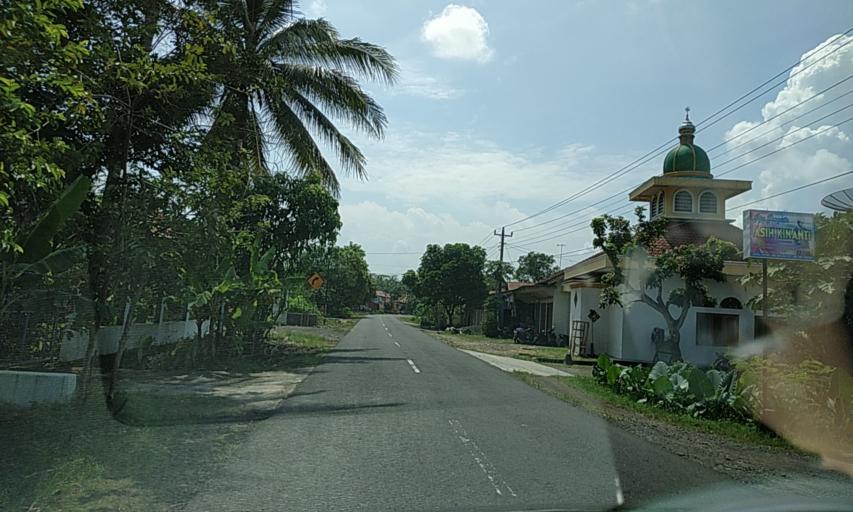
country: ID
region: Central Java
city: Mulyosari
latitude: -7.5223
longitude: 108.7844
